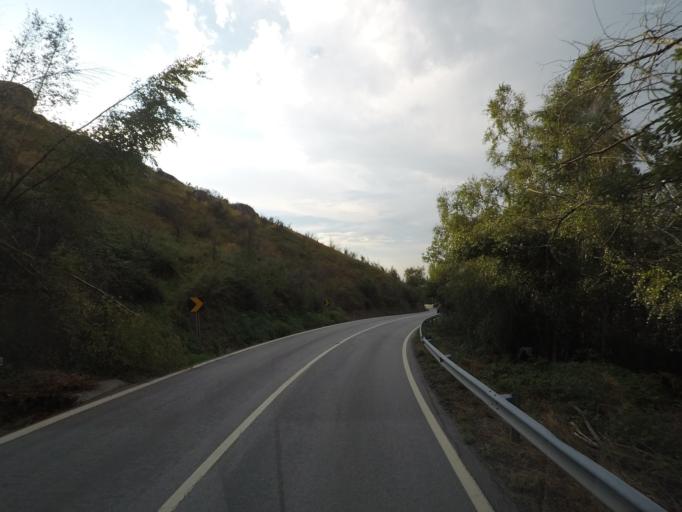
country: PT
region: Porto
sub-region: Baiao
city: Valadares
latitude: 41.1985
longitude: -7.9532
